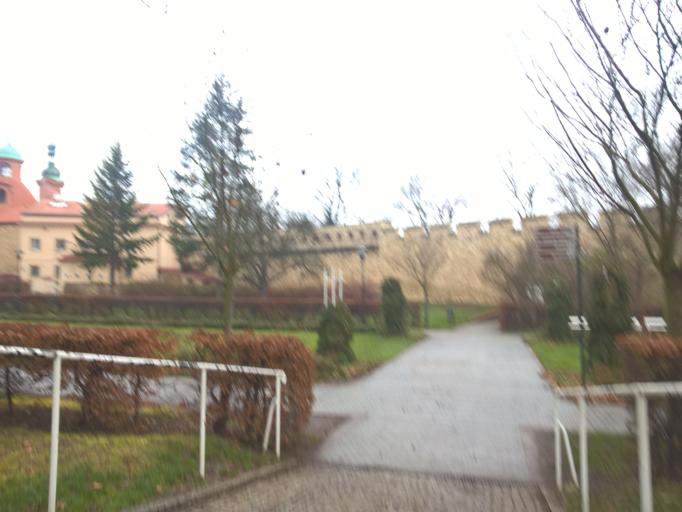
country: CZ
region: Praha
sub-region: Praha 1
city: Mala Strana
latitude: 50.0822
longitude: 14.3965
